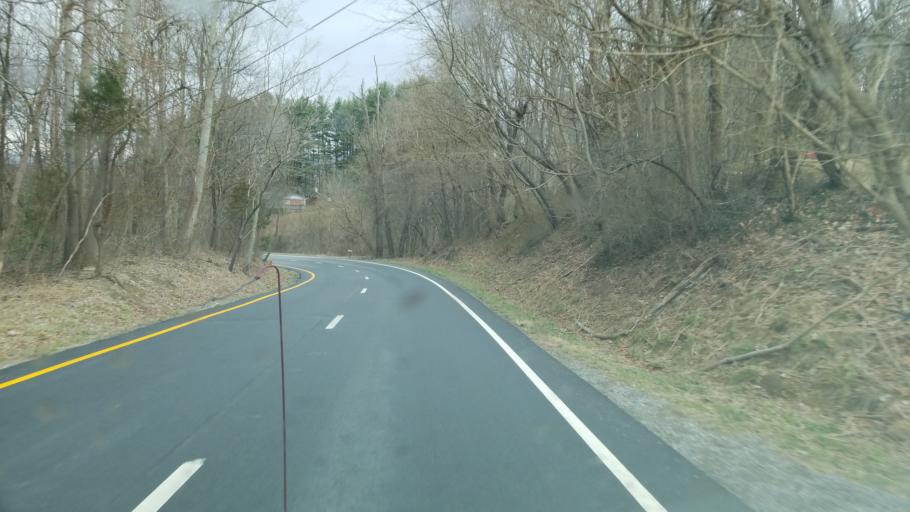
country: US
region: Virginia
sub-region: Giles County
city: Pearisburg
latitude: 37.2963
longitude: -80.7411
